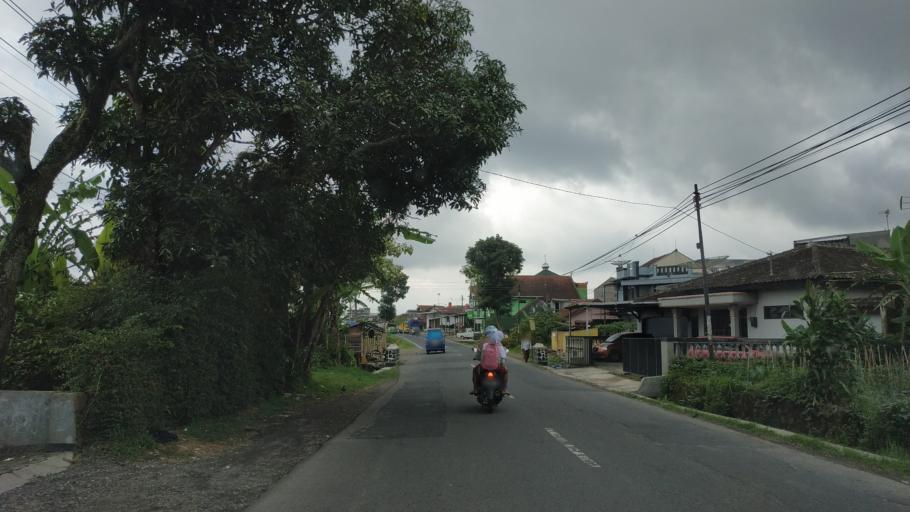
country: ID
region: Central Java
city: Magelang
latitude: -7.2859
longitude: 110.1146
